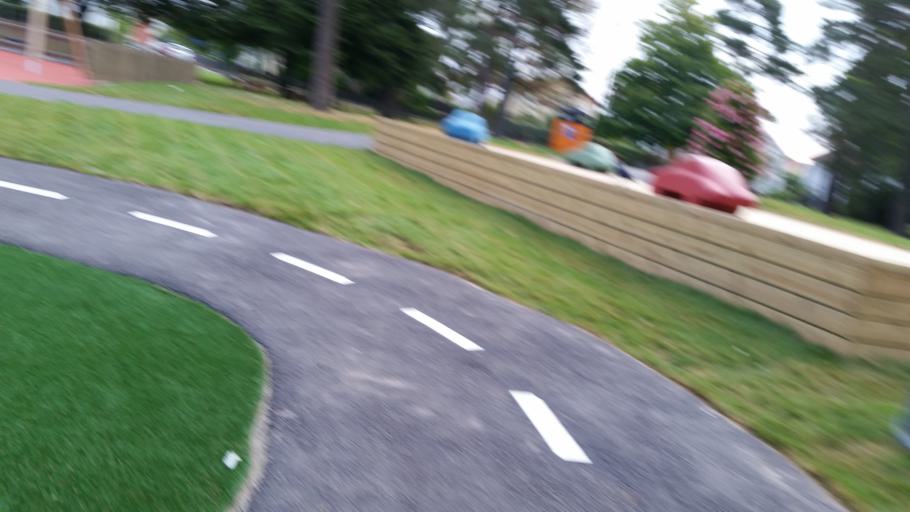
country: SE
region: Vaestra Goetaland
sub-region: Trollhattan
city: Trollhattan
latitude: 58.2838
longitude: 12.2930
